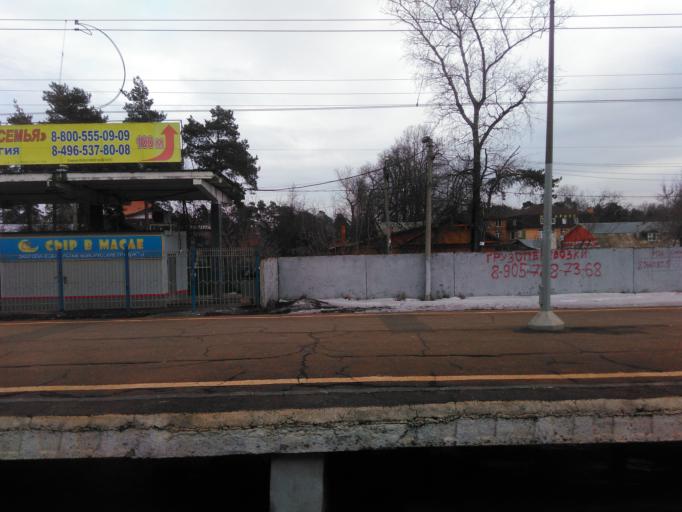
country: RU
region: Moskovskaya
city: Mamontovka
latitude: 55.9782
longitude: 37.8189
